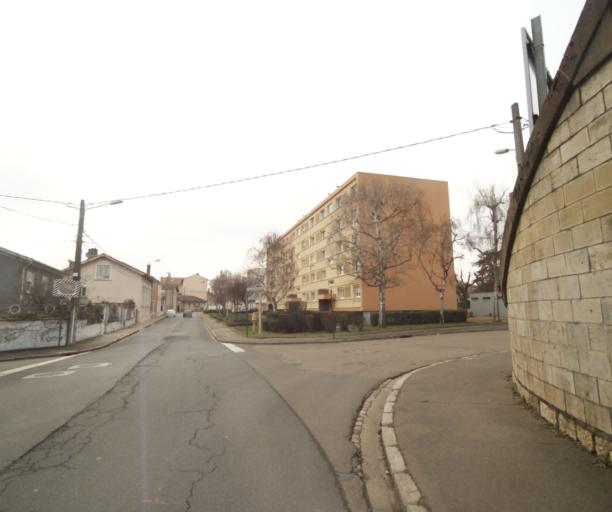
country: FR
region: Rhone-Alpes
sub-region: Departement de la Loire
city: Roanne
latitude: 46.0287
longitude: 4.0742
